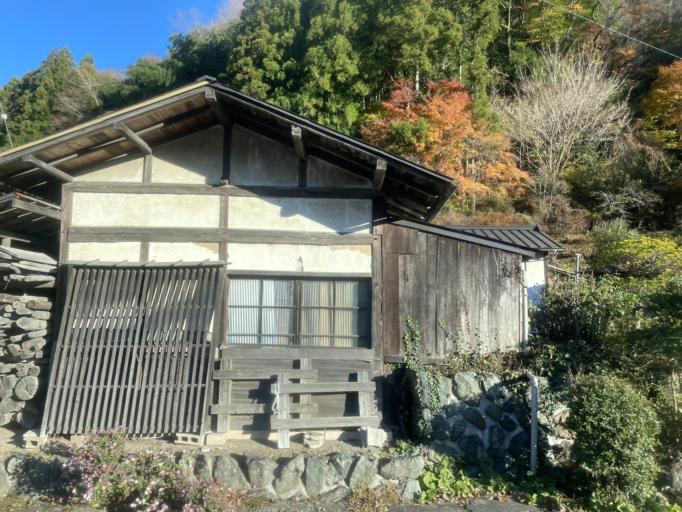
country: JP
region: Saitama
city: Yorii
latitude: 36.0545
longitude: 139.1788
